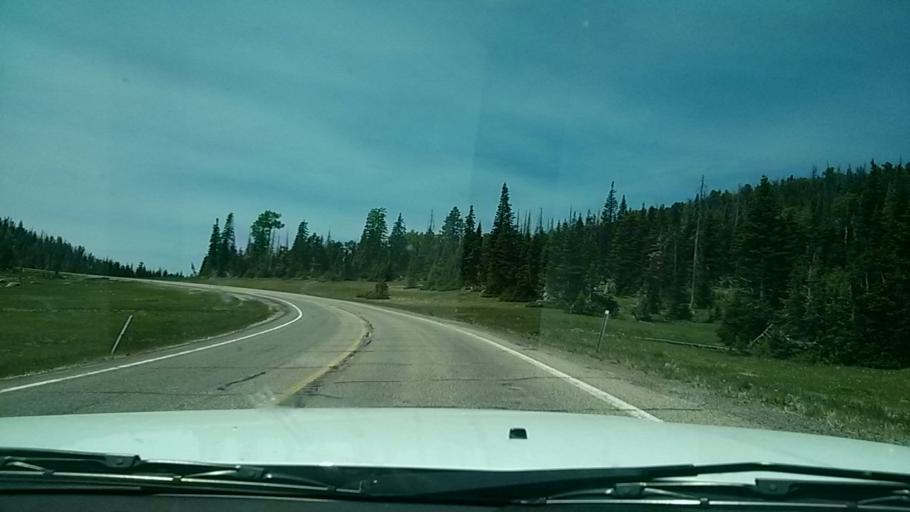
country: US
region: Utah
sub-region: Iron County
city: Cedar City
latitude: 37.5715
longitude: -112.8394
